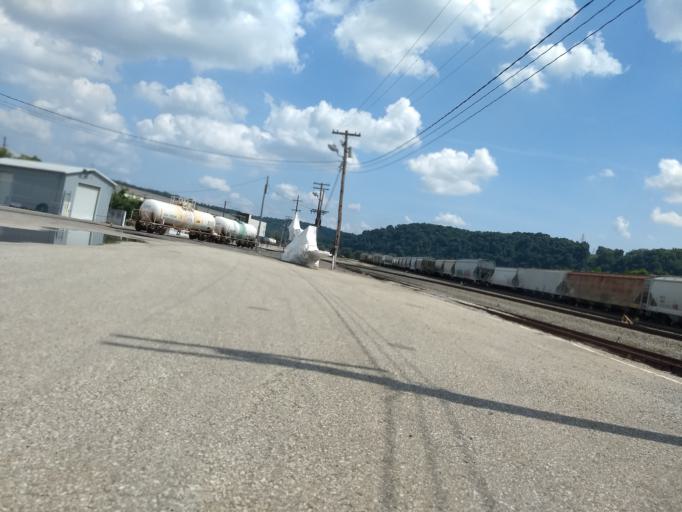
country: US
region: Pennsylvania
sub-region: Allegheny County
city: Homestead
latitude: 40.4042
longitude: -79.9472
